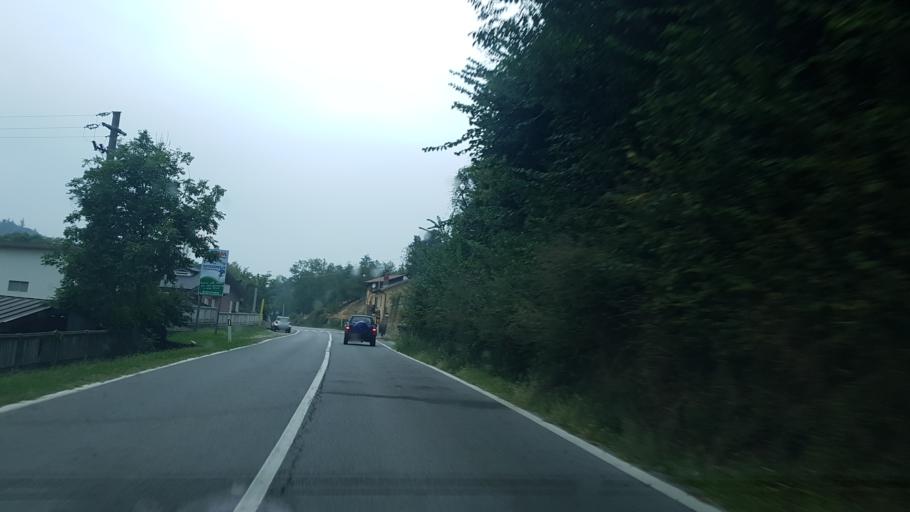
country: IT
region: Piedmont
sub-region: Provincia di Cuneo
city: Frabosa Sottana
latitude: 44.3253
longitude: 7.7999
